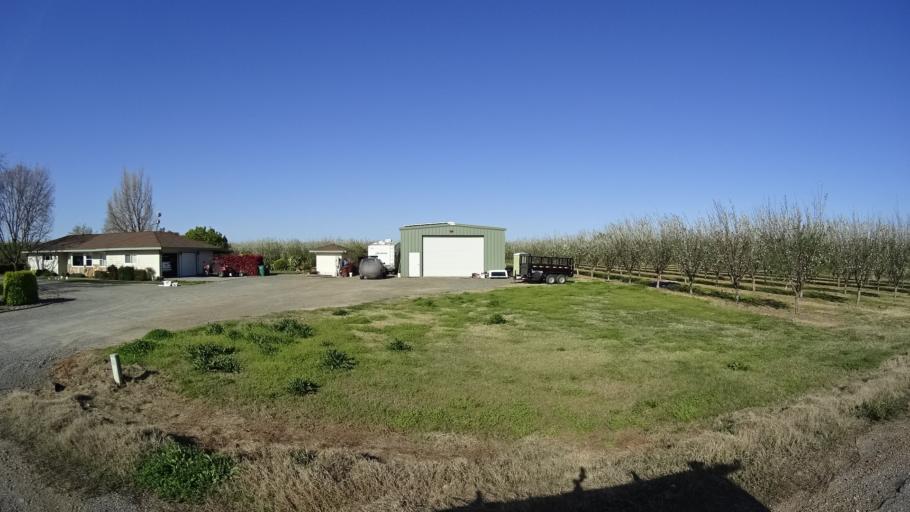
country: US
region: California
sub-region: Glenn County
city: Orland
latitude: 39.7653
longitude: -122.1227
